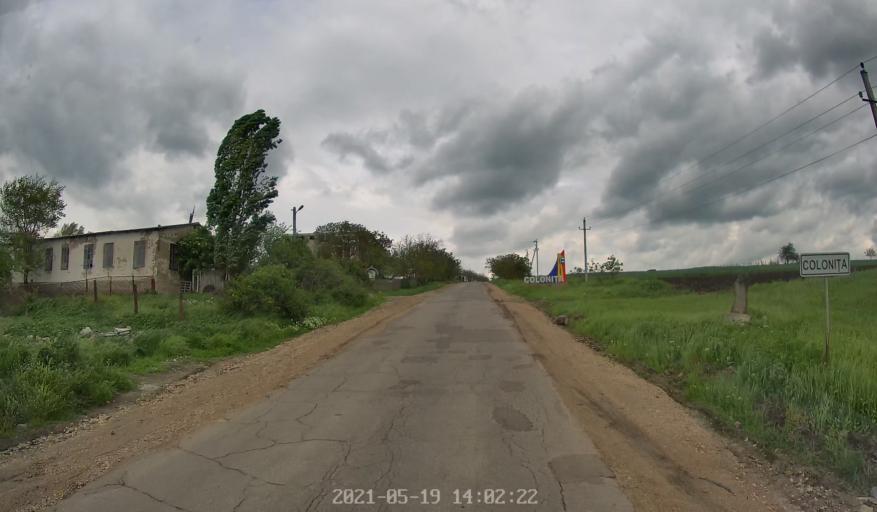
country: MD
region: Chisinau
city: Chisinau
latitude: 47.0349
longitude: 28.9440
